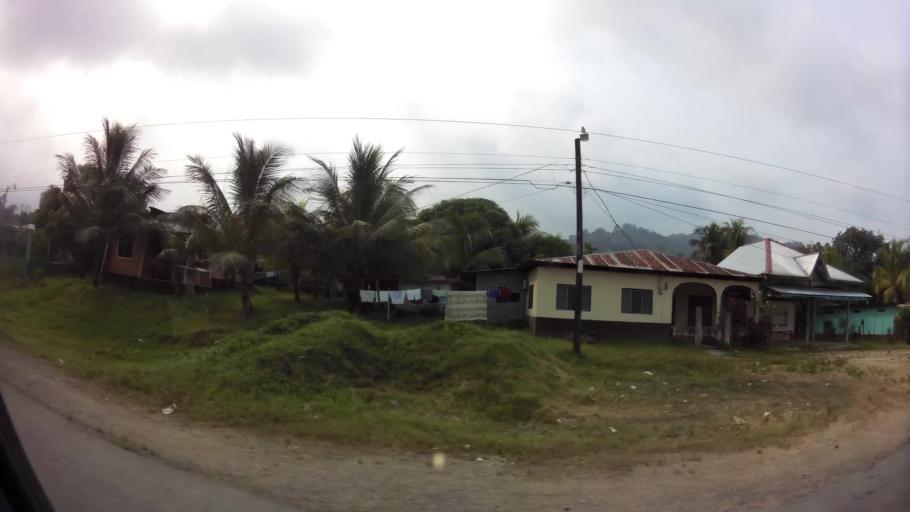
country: HN
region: Yoro
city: Toyos
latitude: 15.5252
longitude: -87.6565
